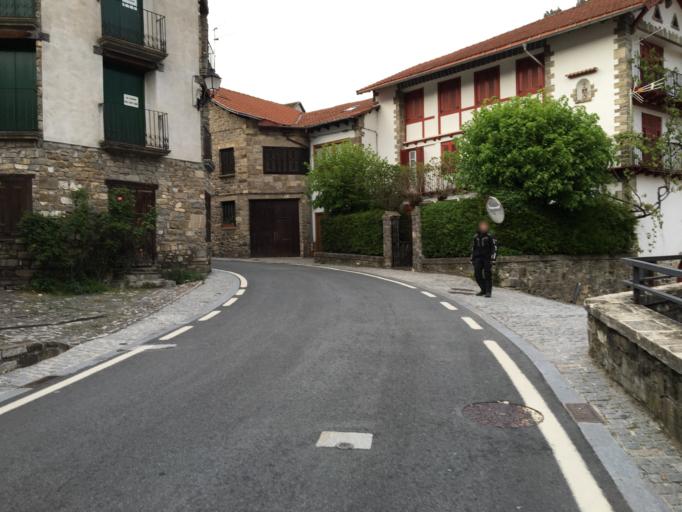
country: ES
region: Navarre
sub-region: Provincia de Navarra
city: Urzainqui
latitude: 42.8609
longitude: -0.9227
